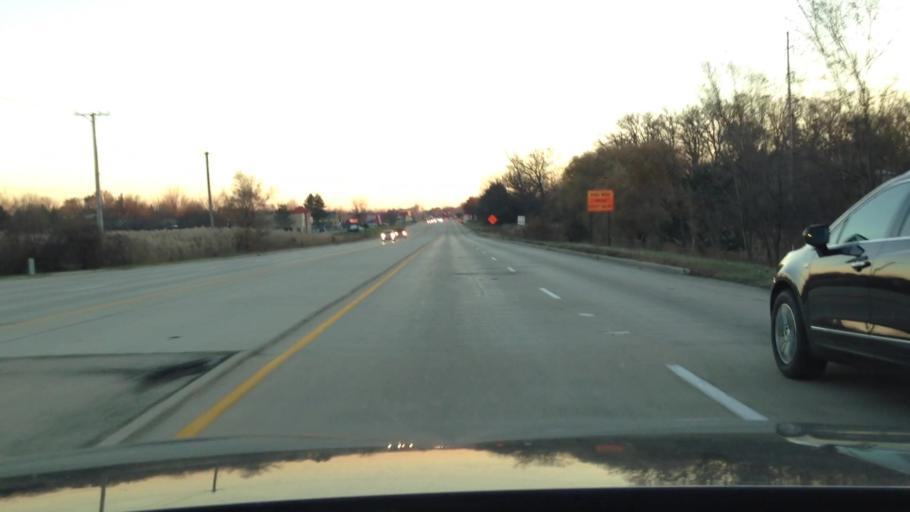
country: US
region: Illinois
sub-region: Cook County
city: Bartlett
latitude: 41.9814
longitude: -88.2073
